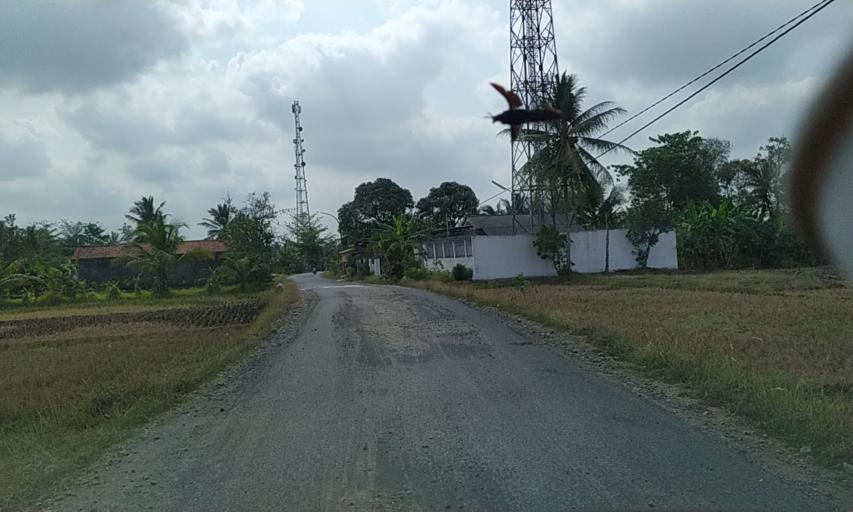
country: ID
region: Central Java
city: Sidareja
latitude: -7.4884
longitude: 108.7871
